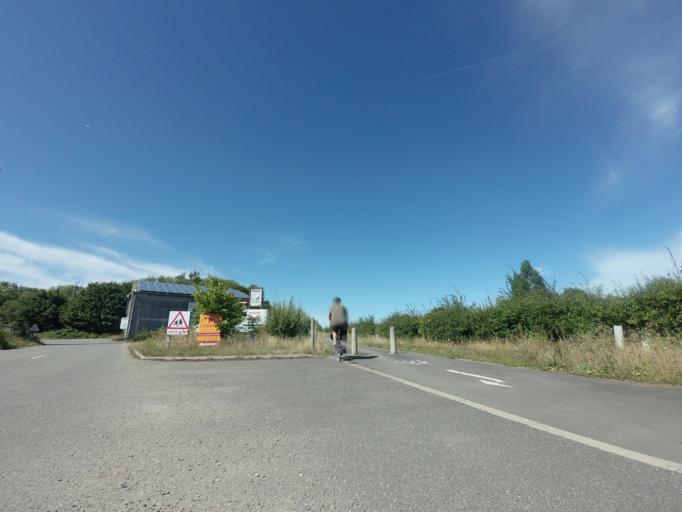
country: GB
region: England
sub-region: Kent
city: Sandwich
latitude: 51.3186
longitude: 1.3463
